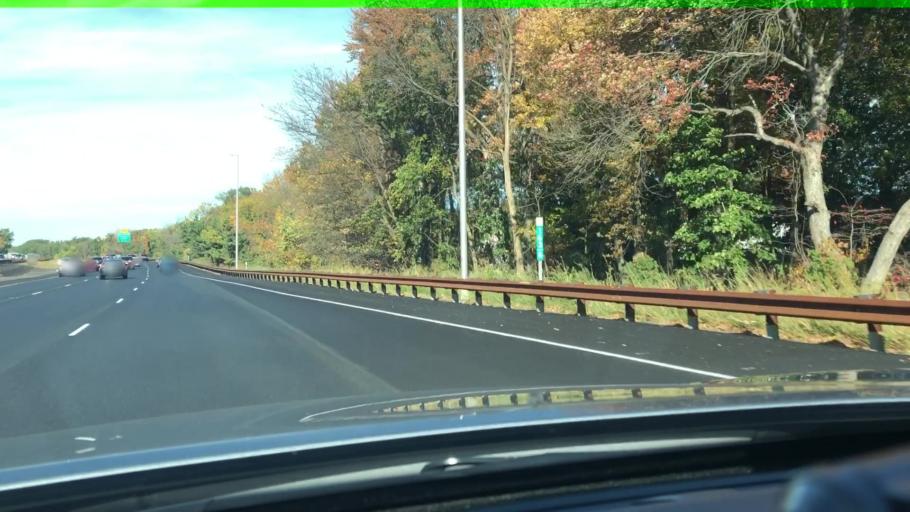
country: US
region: New Jersey
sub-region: Bergen County
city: Paramus
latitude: 40.9442
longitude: -74.0676
